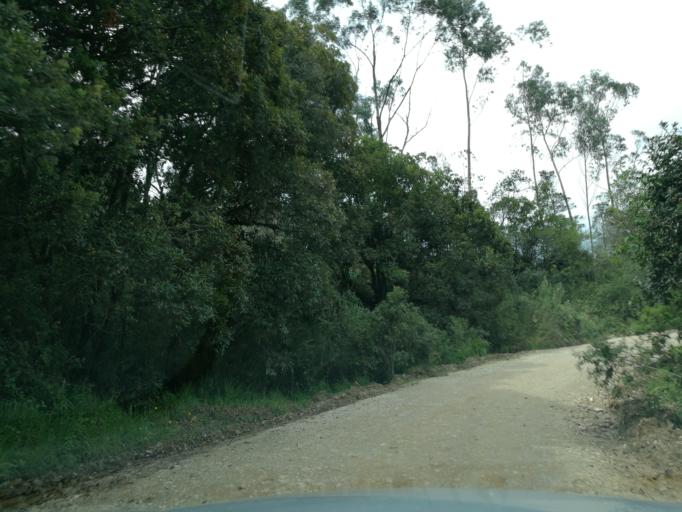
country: CO
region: Boyaca
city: Arcabuco
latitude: 5.7530
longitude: -73.4475
